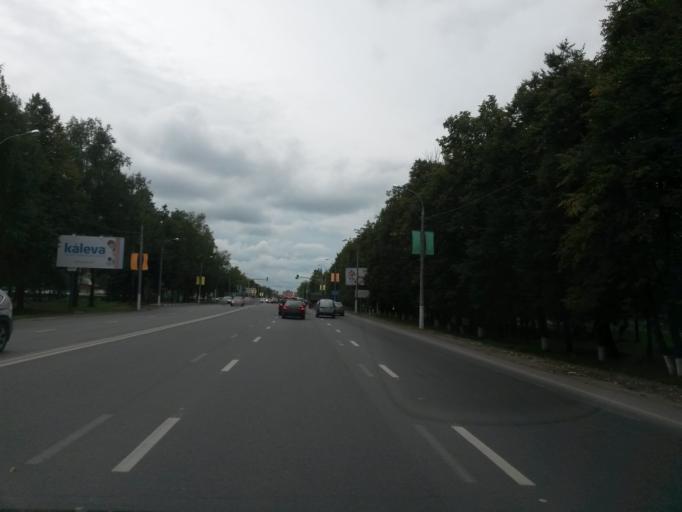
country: RU
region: Moskovskaya
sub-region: Chekhovskiy Rayon
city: Chekhov
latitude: 55.1623
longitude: 37.4660
